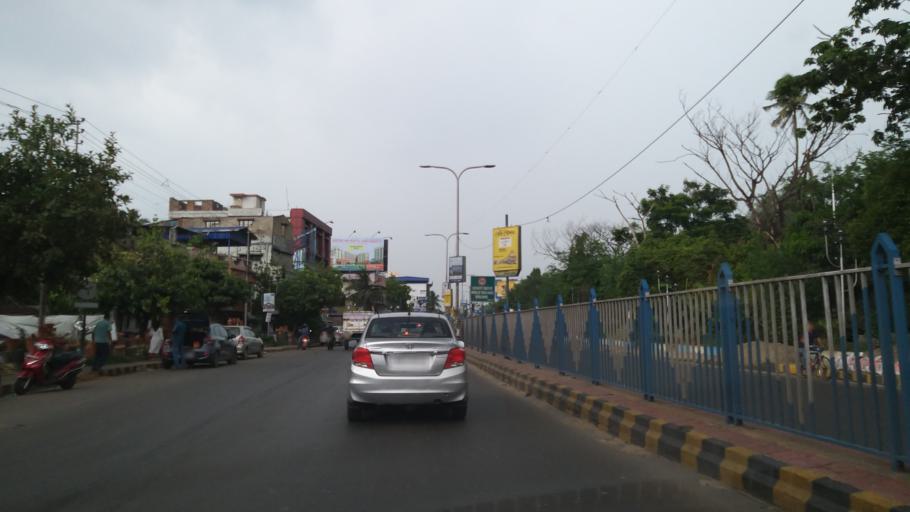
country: IN
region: West Bengal
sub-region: North 24 Parganas
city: Dam Dam
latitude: 22.6546
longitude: 88.4394
